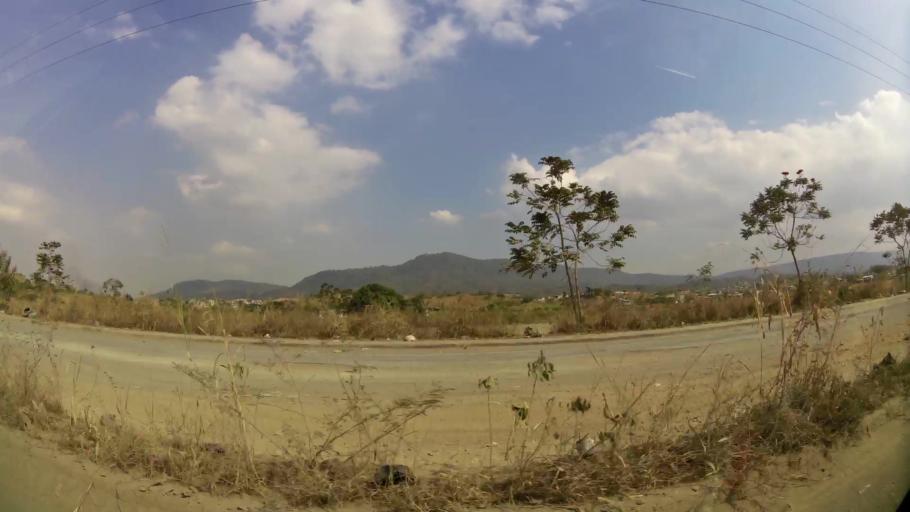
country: EC
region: Guayas
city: Santa Lucia
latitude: -2.1211
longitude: -79.9828
